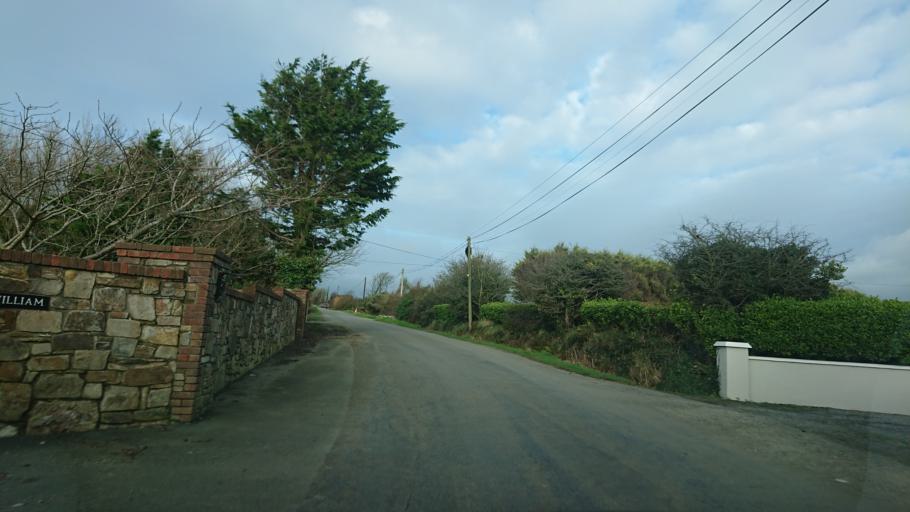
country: IE
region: Munster
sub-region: Waterford
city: Tra Mhor
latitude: 52.1445
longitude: -7.2071
